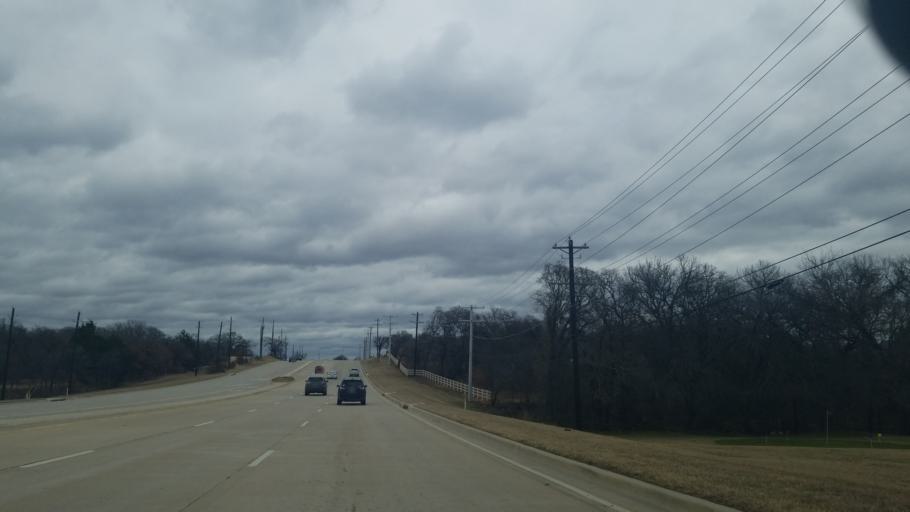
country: US
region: Texas
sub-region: Denton County
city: Bartonville
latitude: 33.0434
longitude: -97.1591
